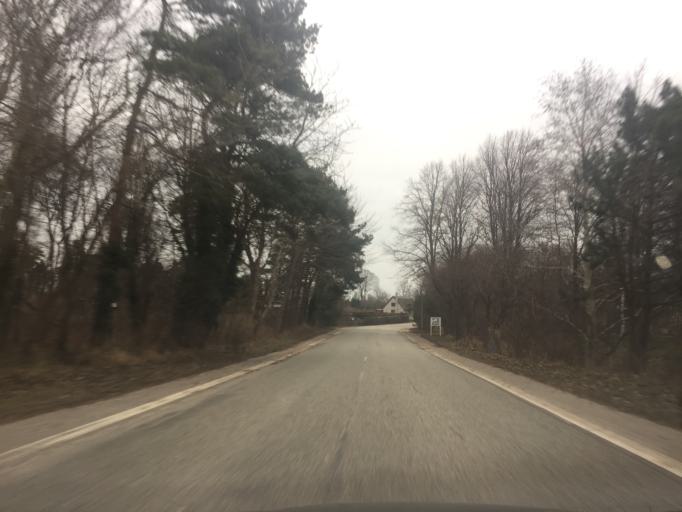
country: DK
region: Capital Region
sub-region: Halsnaes Kommune
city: Liseleje
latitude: 56.0002
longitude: 11.9747
